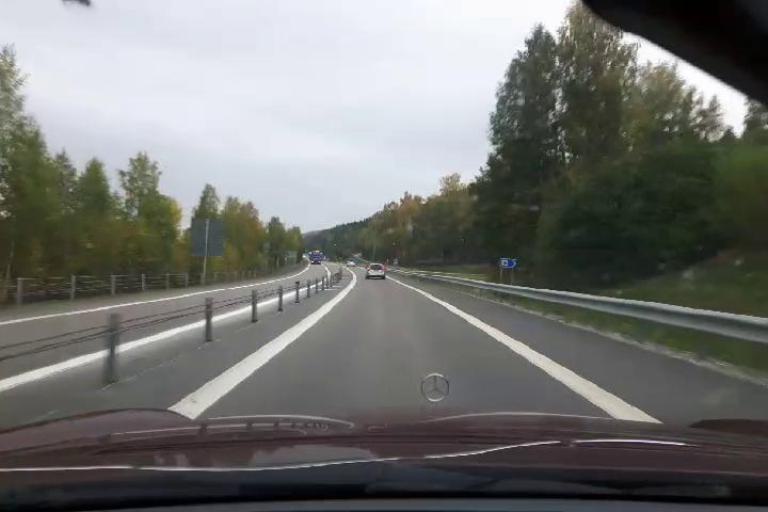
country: SE
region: Vaesternorrland
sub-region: Kramfors Kommun
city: Nordingra
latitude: 63.0461
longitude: 18.3259
